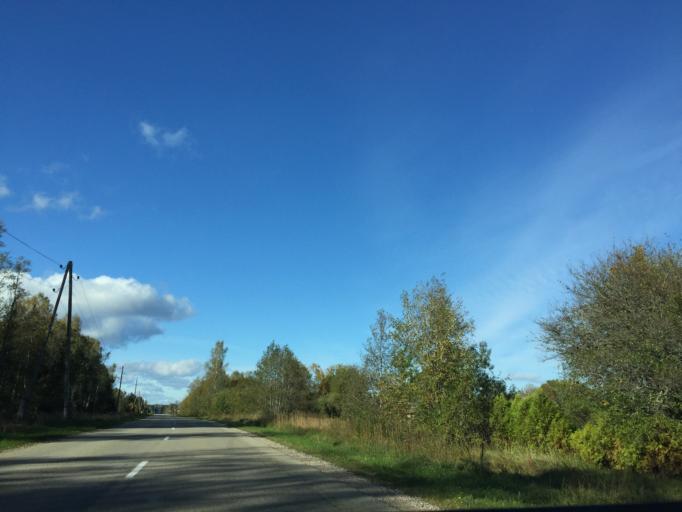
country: LV
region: Rojas
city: Roja
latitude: 57.4468
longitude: 22.8998
